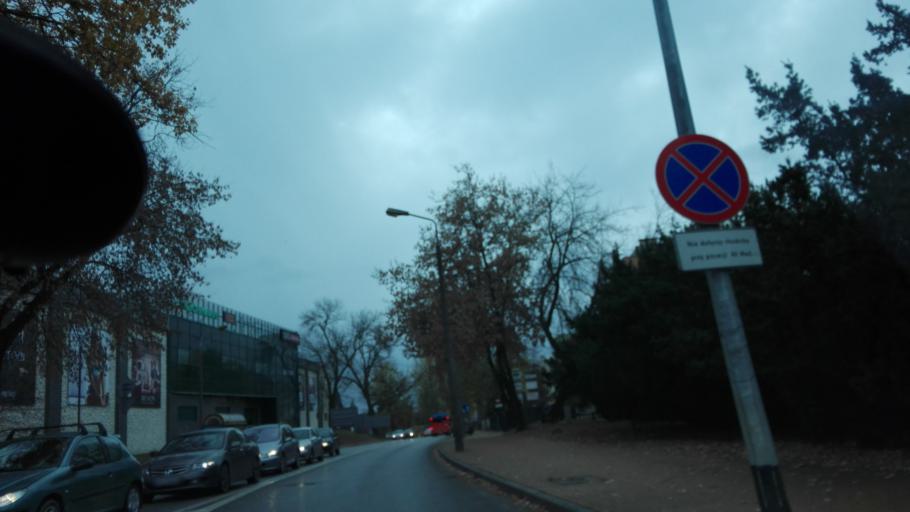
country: PL
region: Lublin Voivodeship
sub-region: Powiat pulawski
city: Pulawy
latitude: 51.4161
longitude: 21.9692
